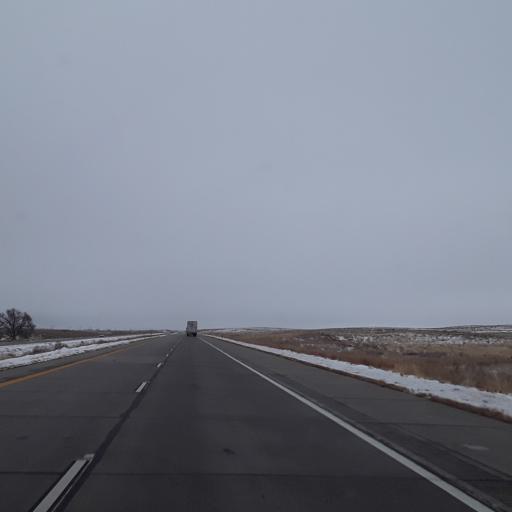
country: US
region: Colorado
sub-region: Logan County
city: Sterling
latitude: 40.5666
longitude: -103.2070
